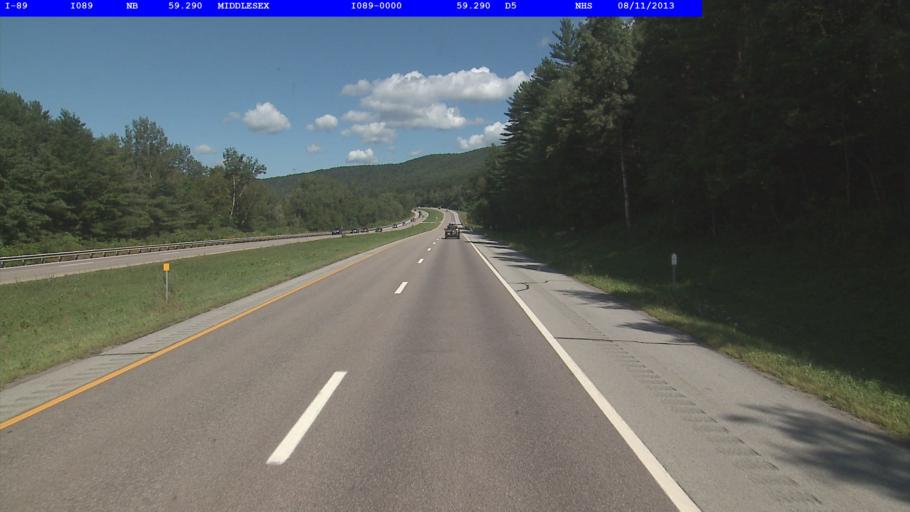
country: US
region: Vermont
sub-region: Washington County
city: Waterbury
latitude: 44.3054
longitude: -72.6905
